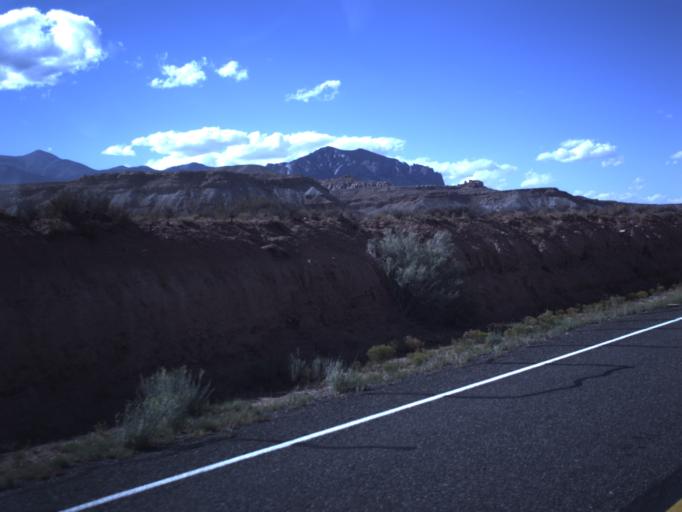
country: US
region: Utah
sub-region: Wayne County
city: Loa
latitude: 38.0932
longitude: -110.6194
